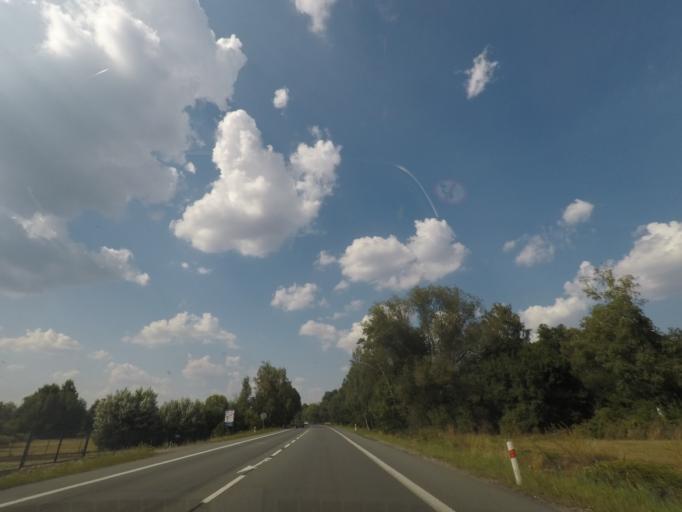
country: CZ
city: Tyniste nad Orlici
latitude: 50.1501
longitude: 16.0692
